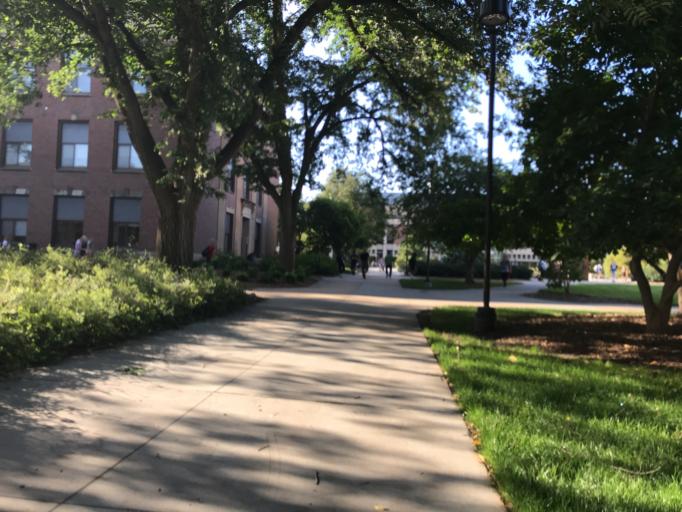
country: US
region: Nebraska
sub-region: Lancaster County
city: Lincoln
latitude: 40.8198
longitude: -96.7024
